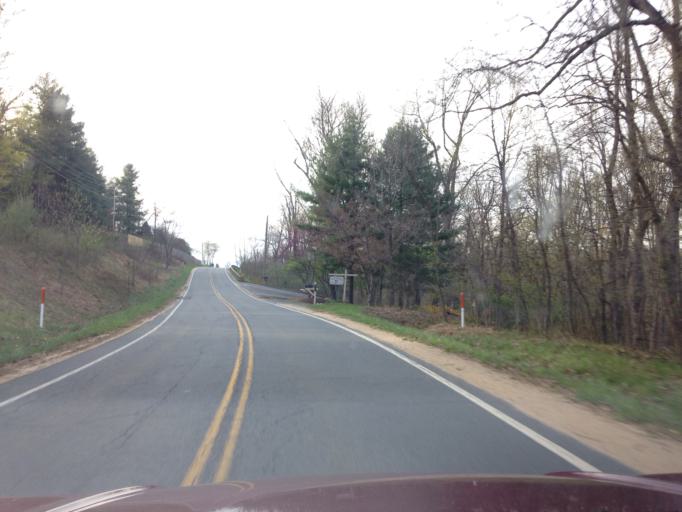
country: US
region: Maryland
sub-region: Frederick County
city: Point of Rocks
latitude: 39.2447
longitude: -77.5592
